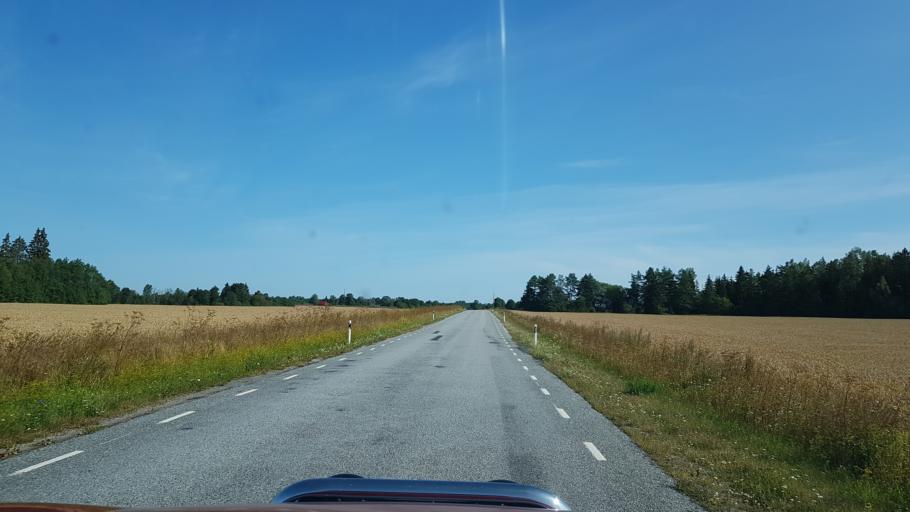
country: EE
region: Harju
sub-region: Raasiku vald
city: Raasiku
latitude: 59.2908
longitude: 25.1686
